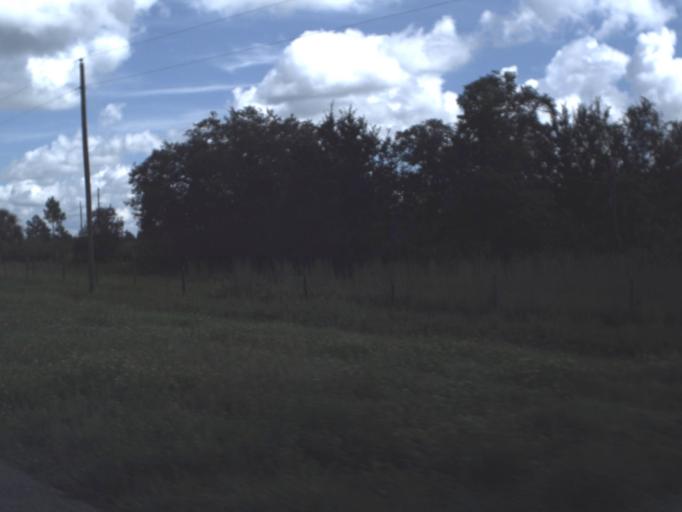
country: US
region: Florida
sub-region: Highlands County
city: Placid Lakes
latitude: 27.0595
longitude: -81.3381
